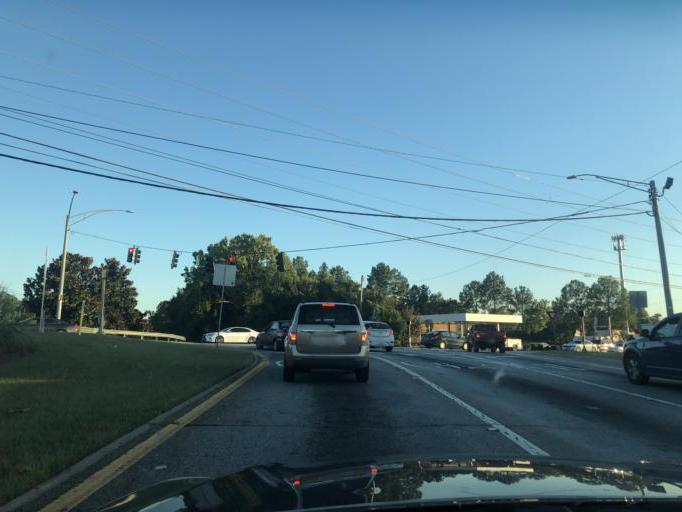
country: US
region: Georgia
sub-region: Muscogee County
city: Columbus
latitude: 32.4624
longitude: -84.9298
